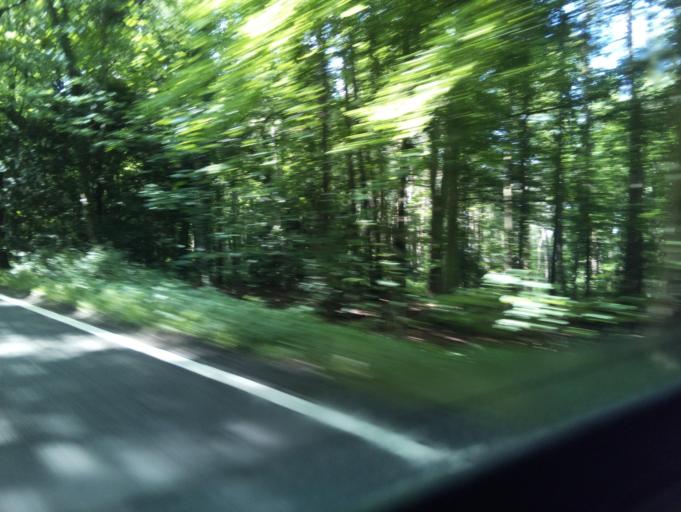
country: GB
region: England
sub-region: North Lincolnshire
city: Manton
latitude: 53.5426
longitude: -0.5770
